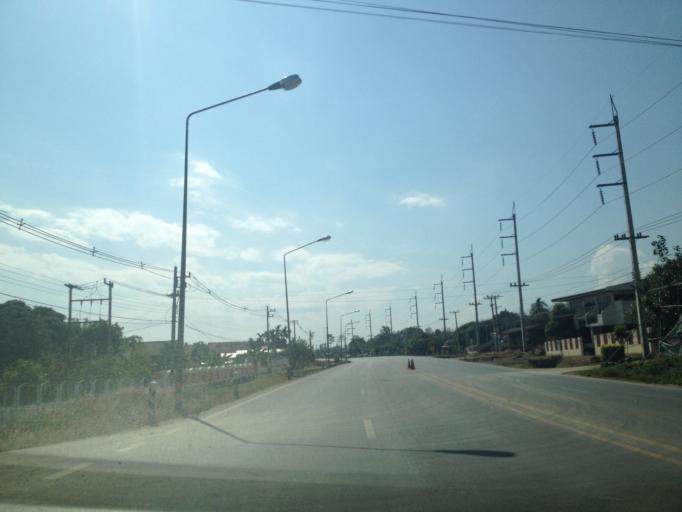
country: TH
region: Chiang Mai
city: Chom Thong
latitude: 18.3610
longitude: 98.6799
